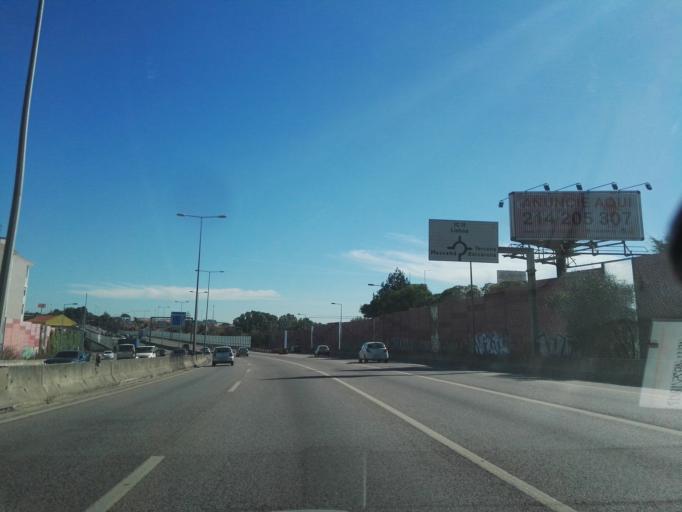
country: PT
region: Lisbon
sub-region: Oeiras
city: Barcarena
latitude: 38.7503
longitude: -9.2858
